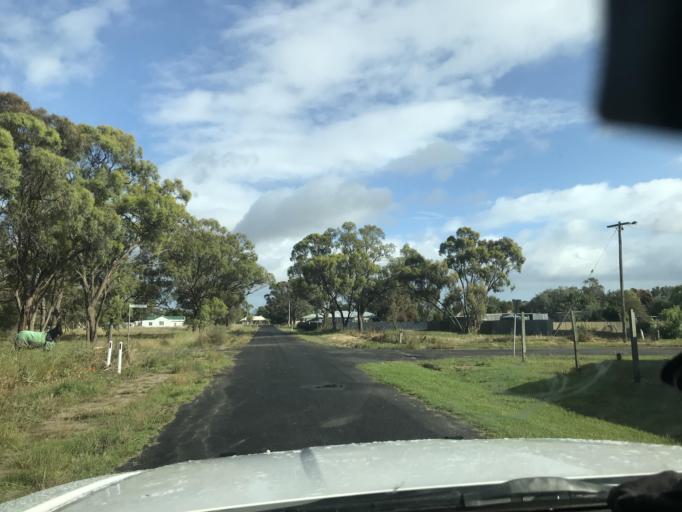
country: AU
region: Victoria
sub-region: Horsham
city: Horsham
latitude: -36.7219
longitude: 141.4712
